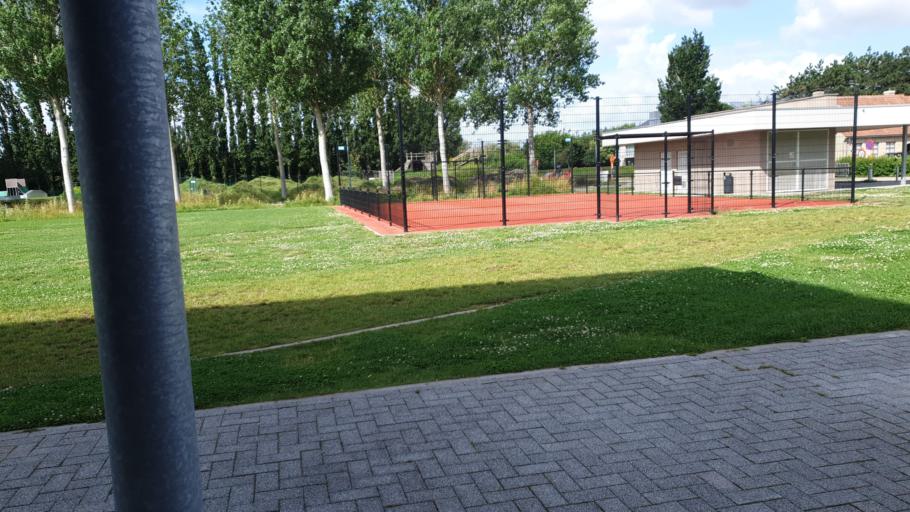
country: BE
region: Flanders
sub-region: Provincie West-Vlaanderen
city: Veurne
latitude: 51.0816
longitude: 2.6600
